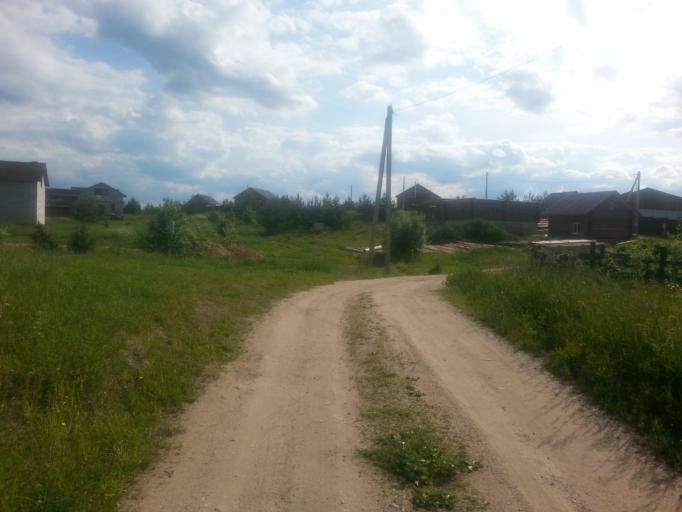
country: BY
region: Minsk
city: Narach
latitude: 54.9759
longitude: 26.6086
